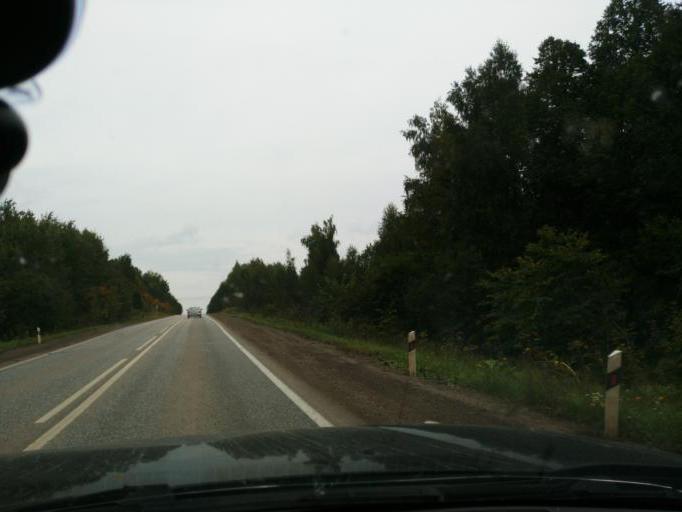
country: RU
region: Perm
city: Chernushka
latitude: 56.5819
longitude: 56.1421
